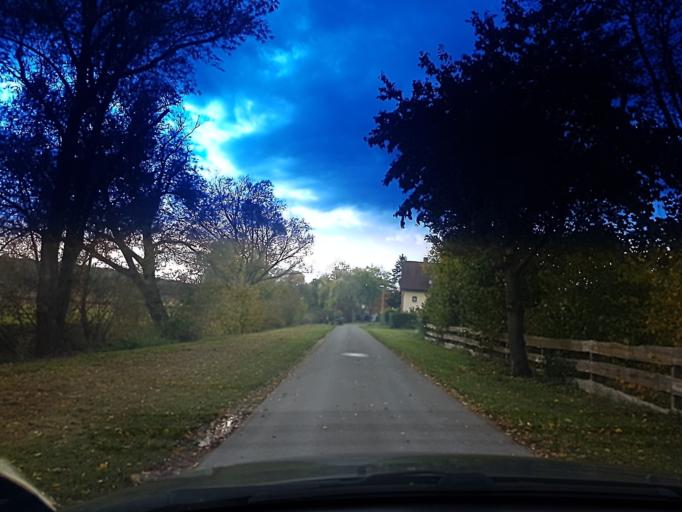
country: DE
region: Bavaria
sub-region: Regierungsbezirk Mittelfranken
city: Muhlhausen
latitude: 49.7489
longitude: 10.7568
